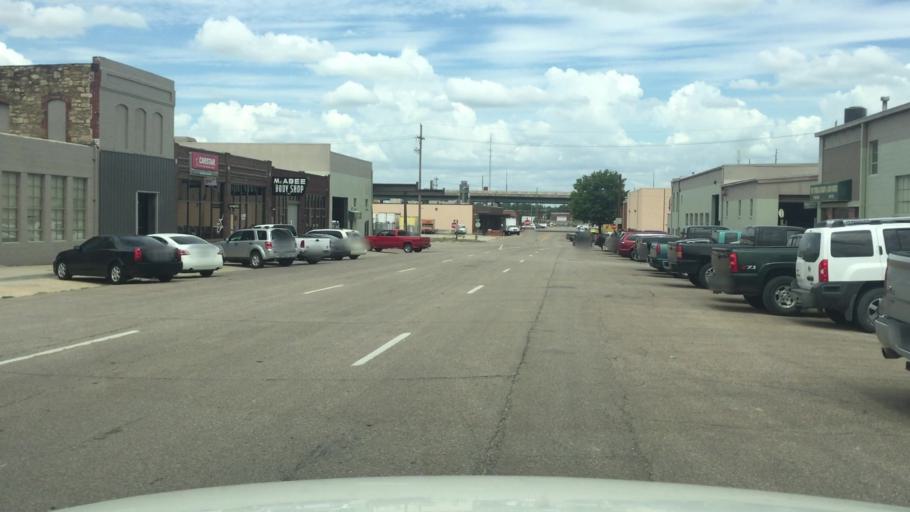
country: US
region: Kansas
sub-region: Shawnee County
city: Topeka
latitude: 39.0552
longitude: -95.6734
